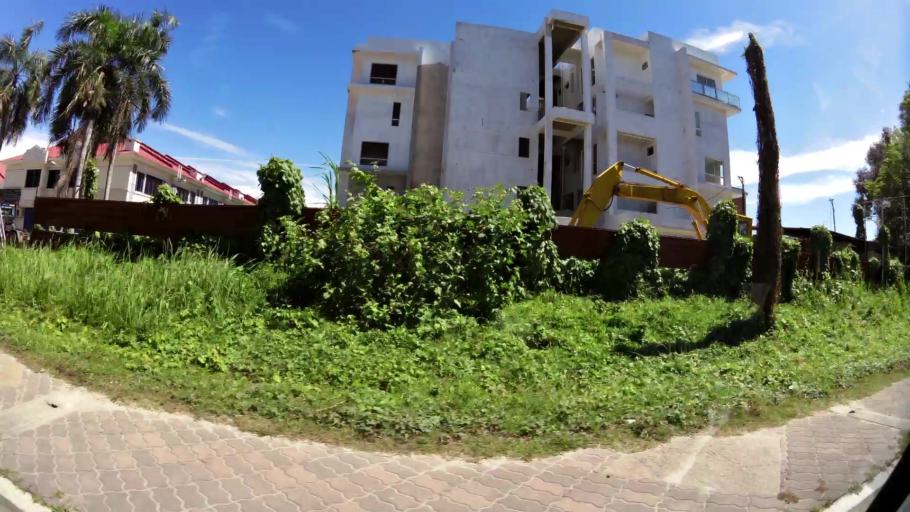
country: BN
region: Brunei and Muara
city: Bandar Seri Begawan
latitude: 5.0291
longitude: 115.0635
